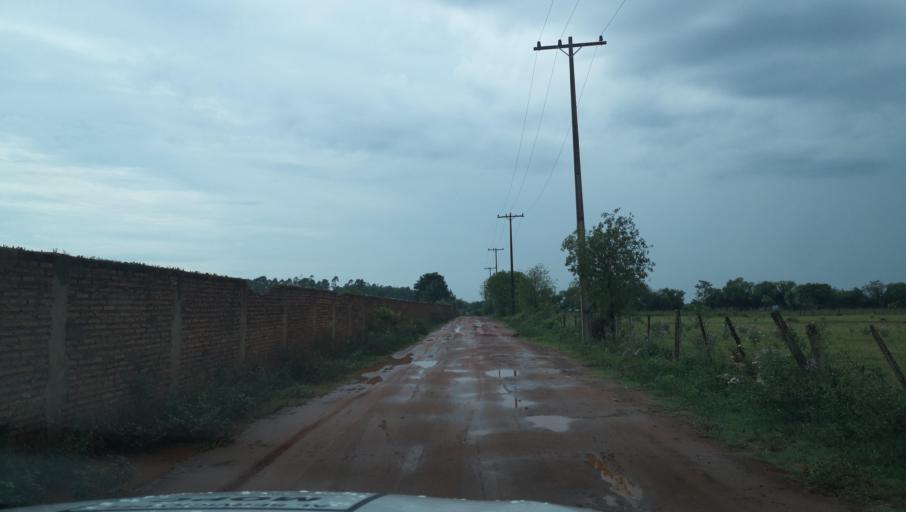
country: PY
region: Misiones
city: Santa Maria
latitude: -26.9016
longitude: -57.0358
